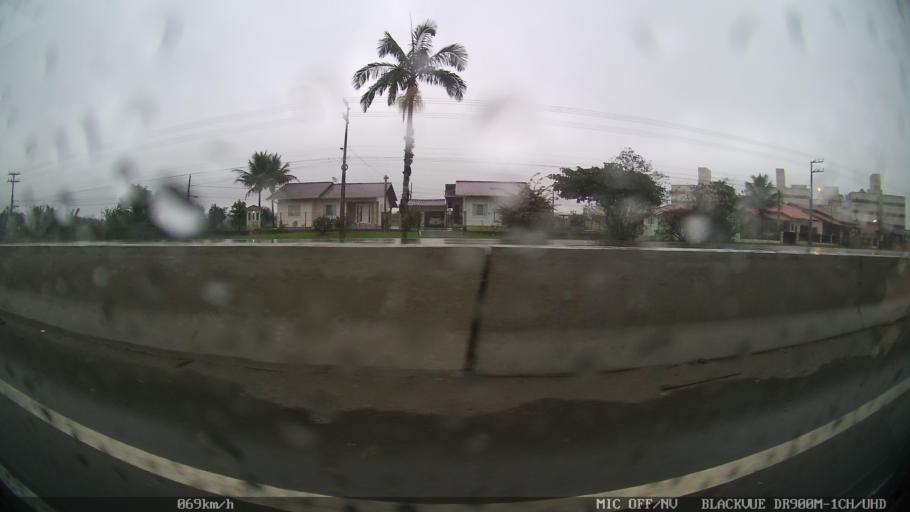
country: BR
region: Santa Catarina
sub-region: Navegantes
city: Navegantes
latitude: -26.8497
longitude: -48.7125
